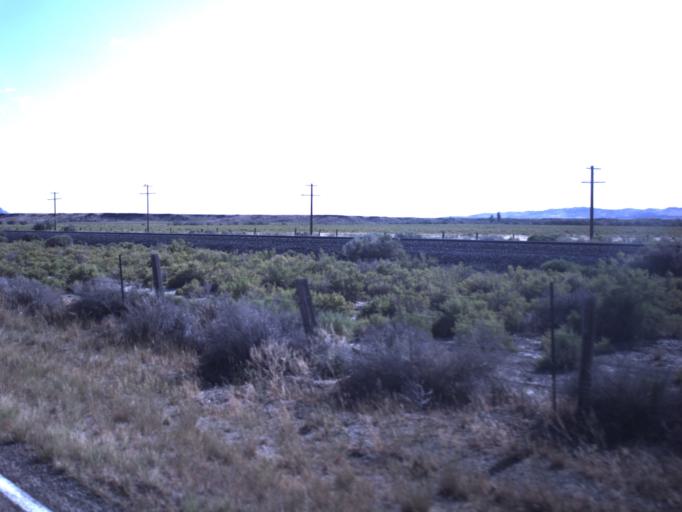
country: US
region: Utah
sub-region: Beaver County
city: Milford
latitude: 38.7045
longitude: -112.9715
